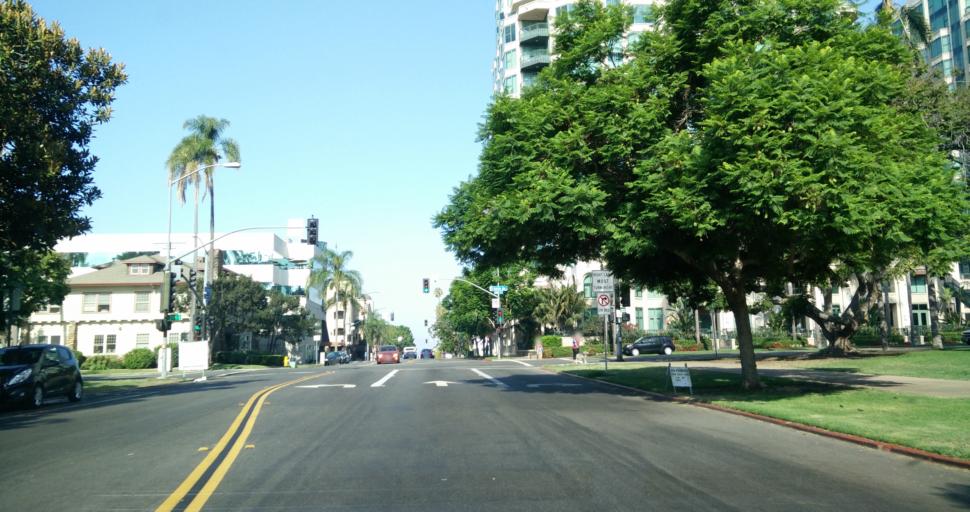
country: US
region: California
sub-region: San Diego County
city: San Diego
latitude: 32.7314
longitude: -117.1588
